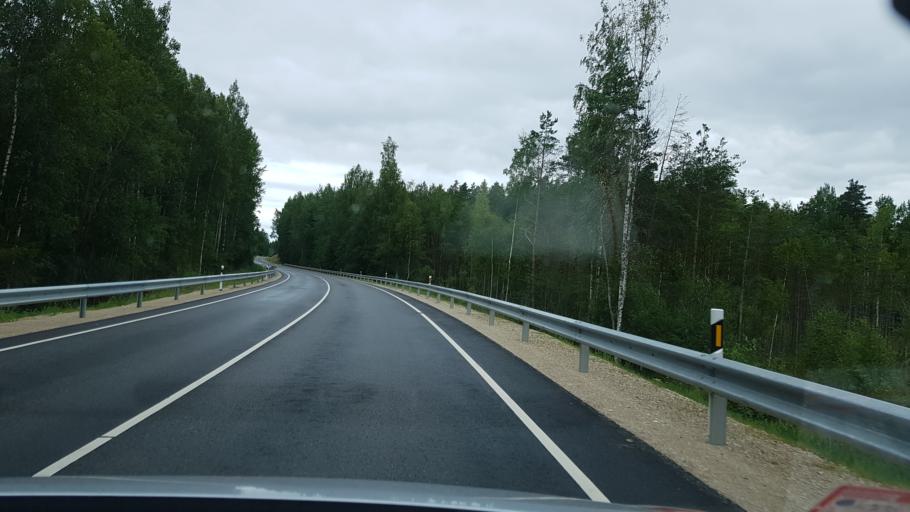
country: EE
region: Polvamaa
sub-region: Raepina vald
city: Rapina
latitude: 58.0801
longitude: 27.3012
